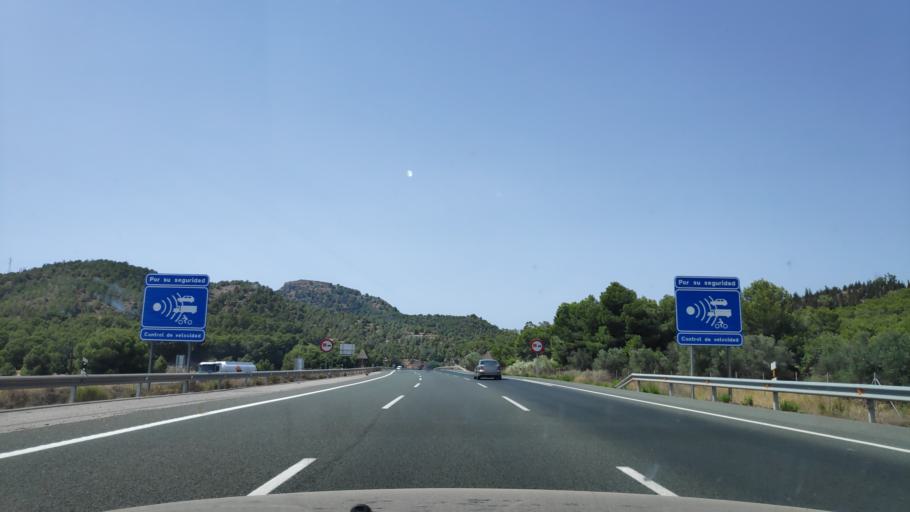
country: ES
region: Murcia
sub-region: Murcia
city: Murcia
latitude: 37.8890
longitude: -1.1404
